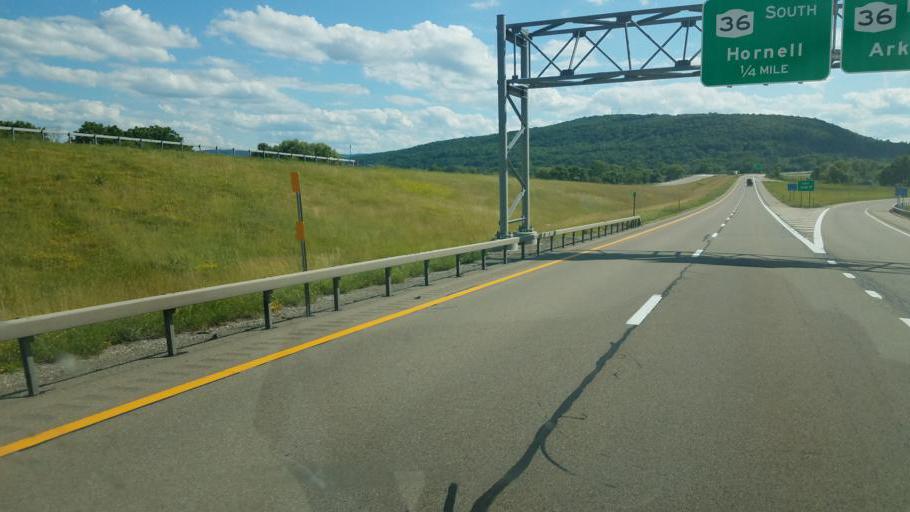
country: US
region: New York
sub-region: Steuben County
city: Hornell
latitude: 42.3750
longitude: -77.6721
